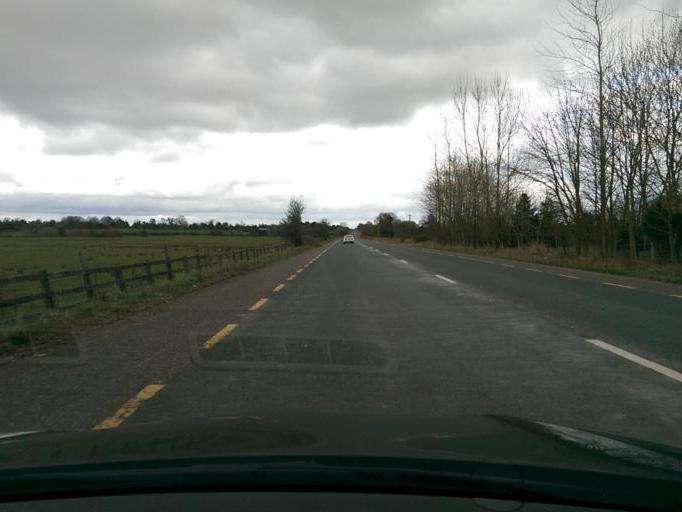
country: IE
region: Leinster
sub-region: Uibh Fhaili
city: Clara
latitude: 53.3982
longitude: -7.6361
